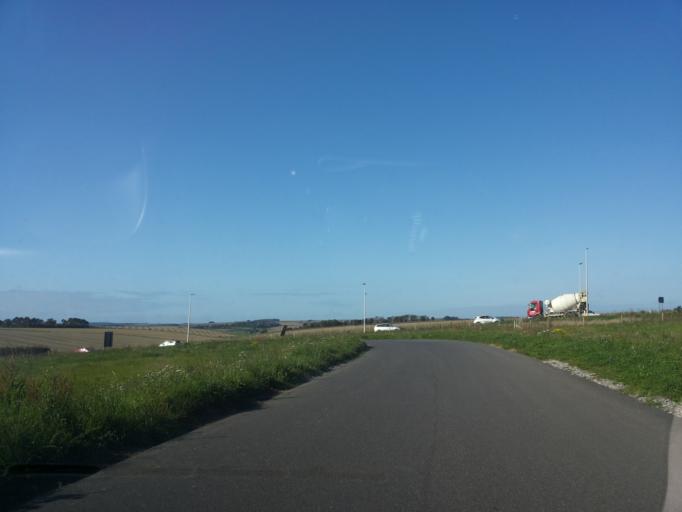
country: GB
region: England
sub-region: Wiltshire
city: Winterbourne Stoke
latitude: 51.1849
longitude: -1.8589
